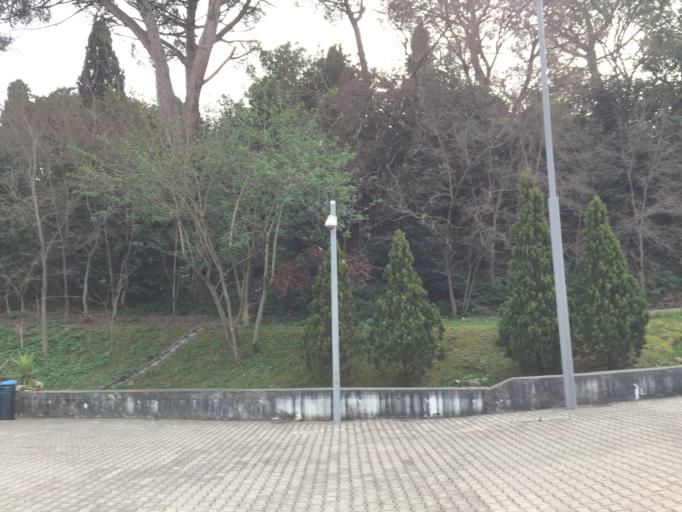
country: VA
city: Vatican City
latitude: 41.8945
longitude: 12.4547
